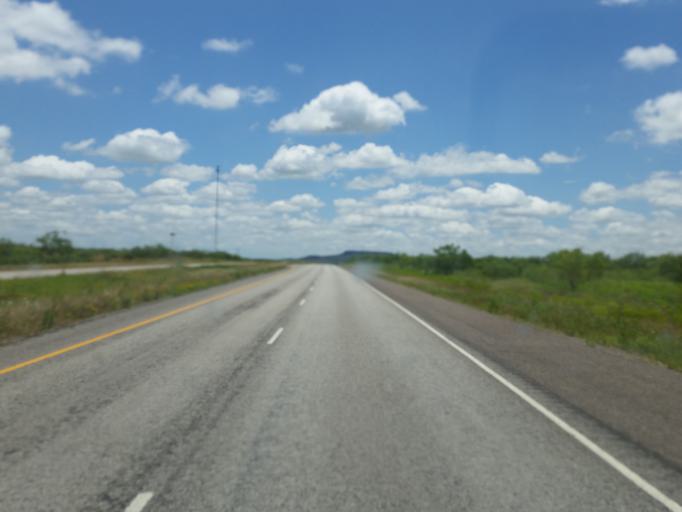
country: US
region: Texas
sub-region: Garza County
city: Post
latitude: 32.9872
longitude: -101.1347
